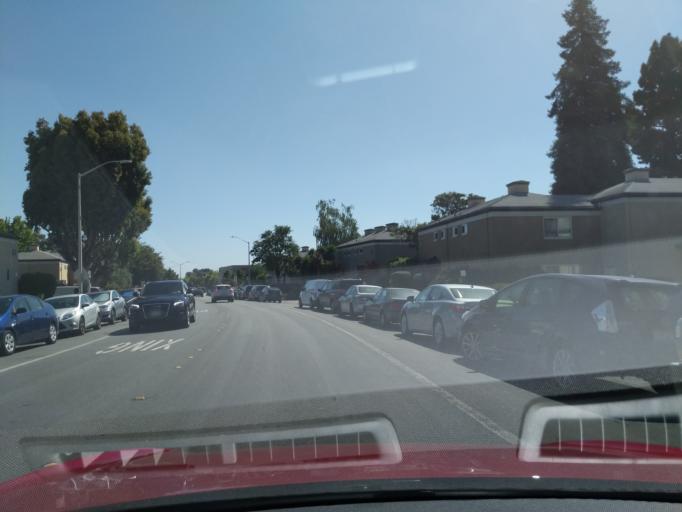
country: US
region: California
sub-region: San Mateo County
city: Belmont
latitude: 37.5342
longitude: -122.3015
